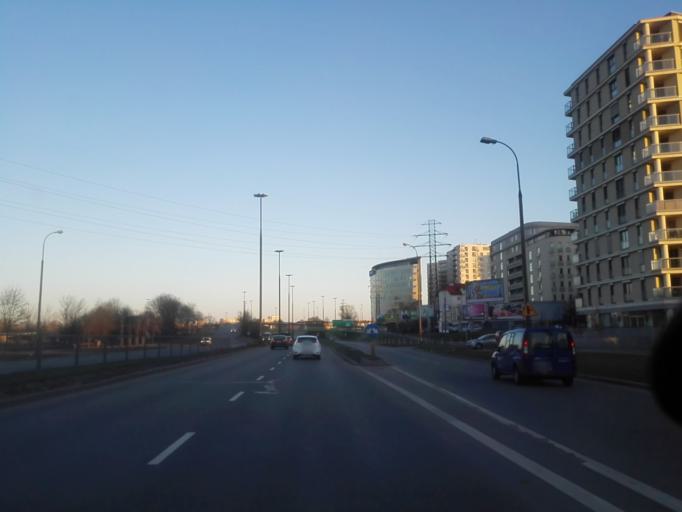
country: PL
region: Masovian Voivodeship
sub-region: Warszawa
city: Mokotow
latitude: 52.1686
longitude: 21.0114
